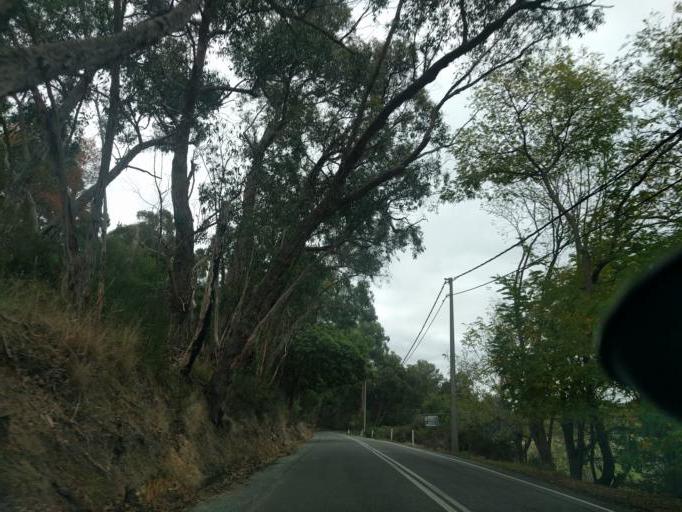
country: AU
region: South Australia
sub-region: Adelaide Hills
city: Stirling
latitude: -35.0370
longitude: 138.7624
